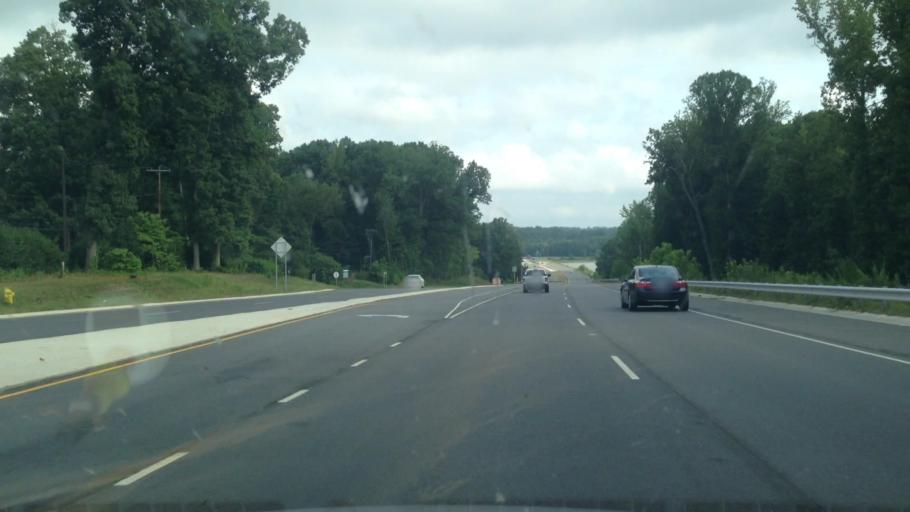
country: US
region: North Carolina
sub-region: Guilford County
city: Summerfield
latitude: 36.1651
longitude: -79.8782
